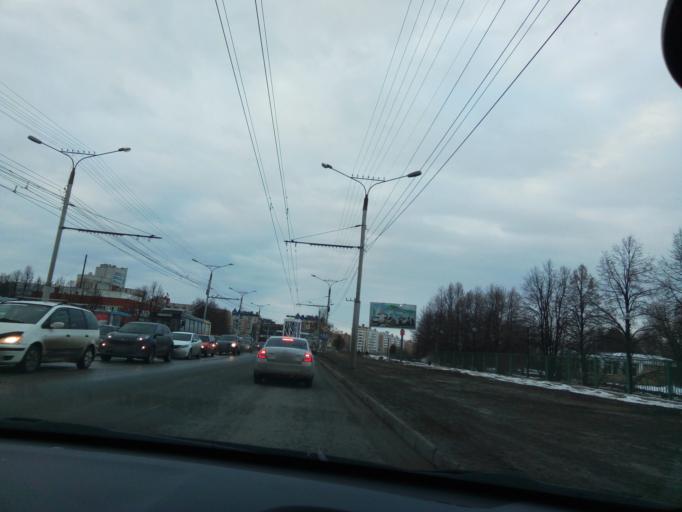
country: RU
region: Chuvashia
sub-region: Cheboksarskiy Rayon
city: Cheboksary
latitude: 56.1458
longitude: 47.2039
